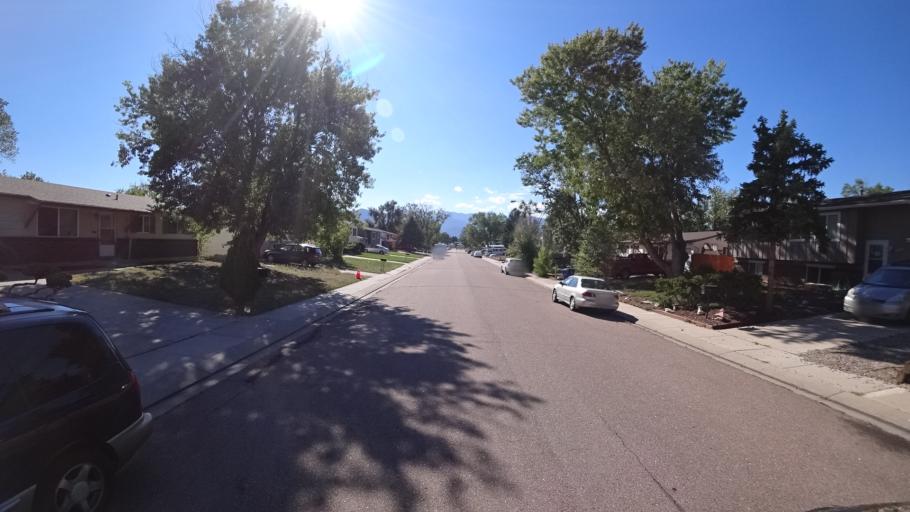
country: US
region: Colorado
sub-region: El Paso County
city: Stratmoor
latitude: 38.7947
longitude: -104.7433
